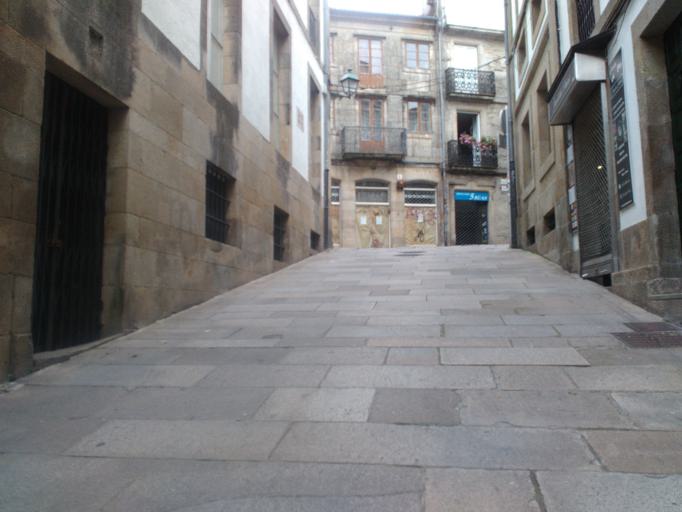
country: ES
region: Galicia
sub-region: Provincia da Coruna
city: Santiago de Compostela
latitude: 42.8797
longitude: -8.5426
